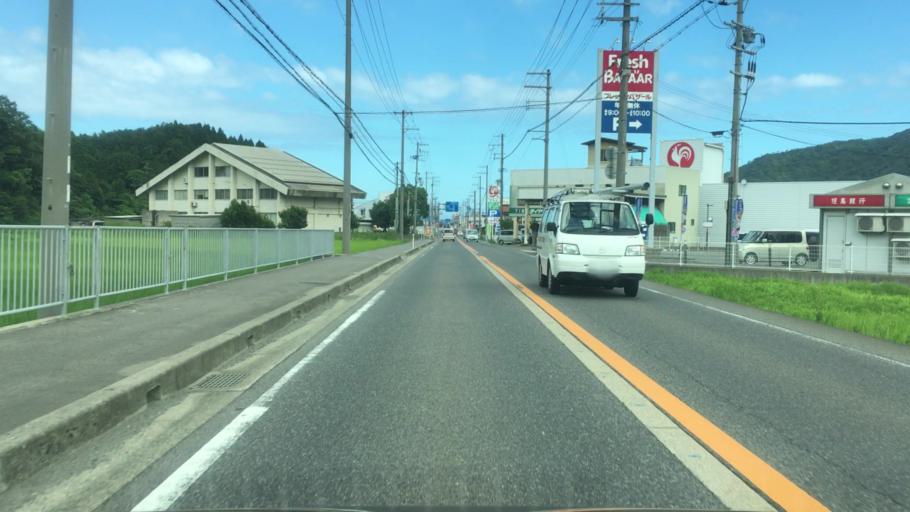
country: JP
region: Tottori
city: Tottori
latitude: 35.6154
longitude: 134.4654
